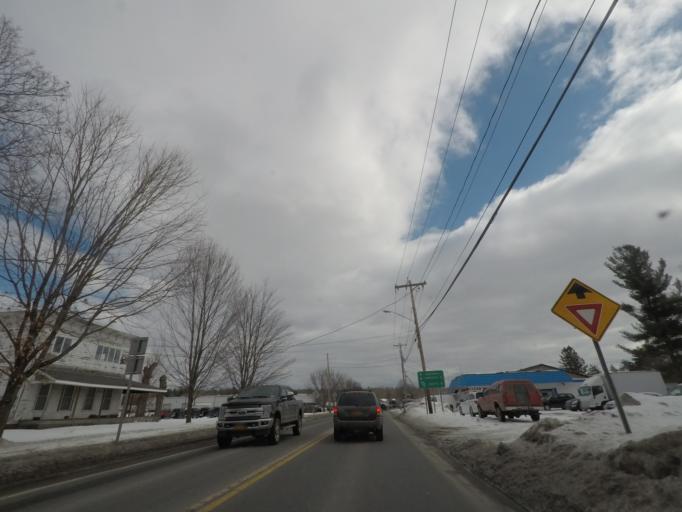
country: US
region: New York
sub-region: Washington County
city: Greenwich
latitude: 43.1038
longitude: -73.5210
